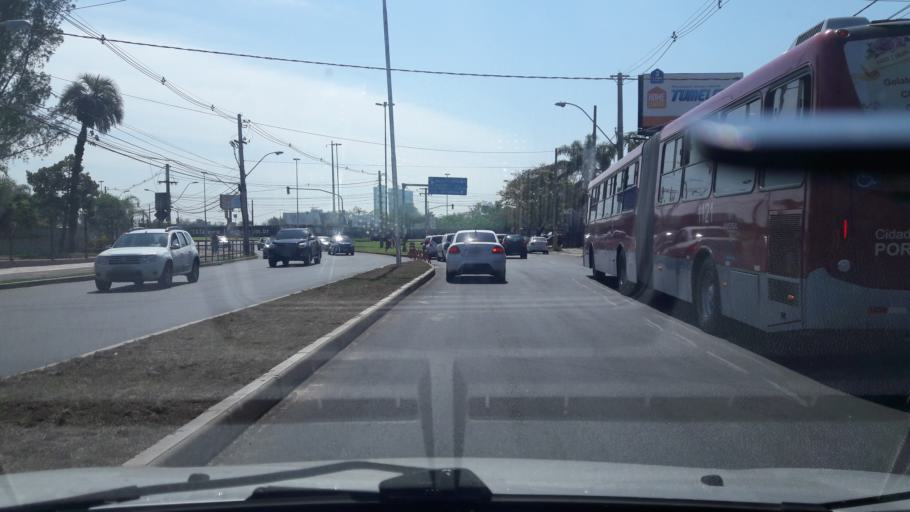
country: BR
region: Rio Grande do Sul
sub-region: Porto Alegre
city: Porto Alegre
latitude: -30.0987
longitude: -51.2482
